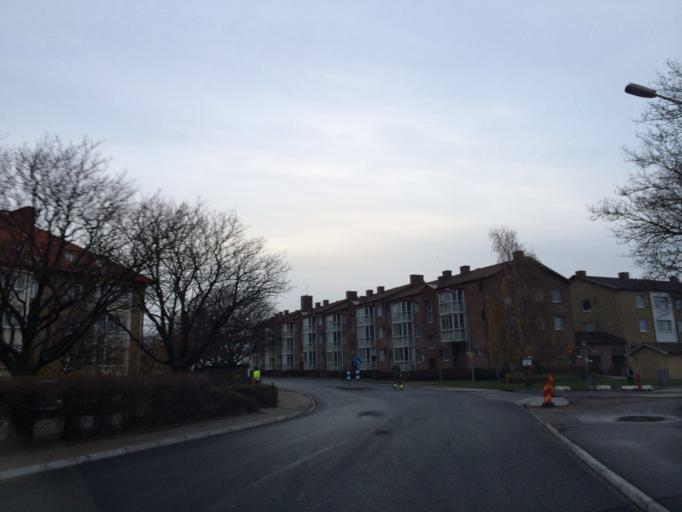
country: SE
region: Skane
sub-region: Lomma Kommun
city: Lomma
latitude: 55.6785
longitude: 13.0741
